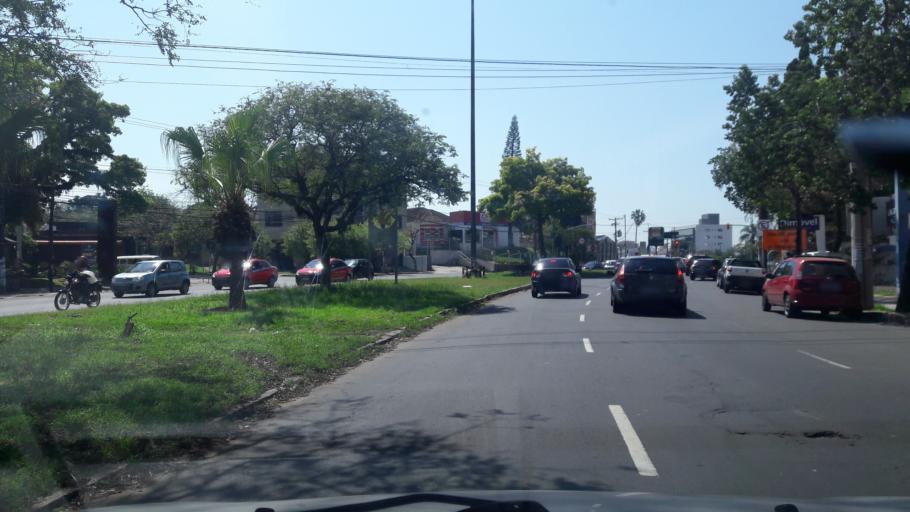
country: BR
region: Rio Grande do Sul
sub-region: Guaiba
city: Guaiba
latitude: -30.1042
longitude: -51.2532
